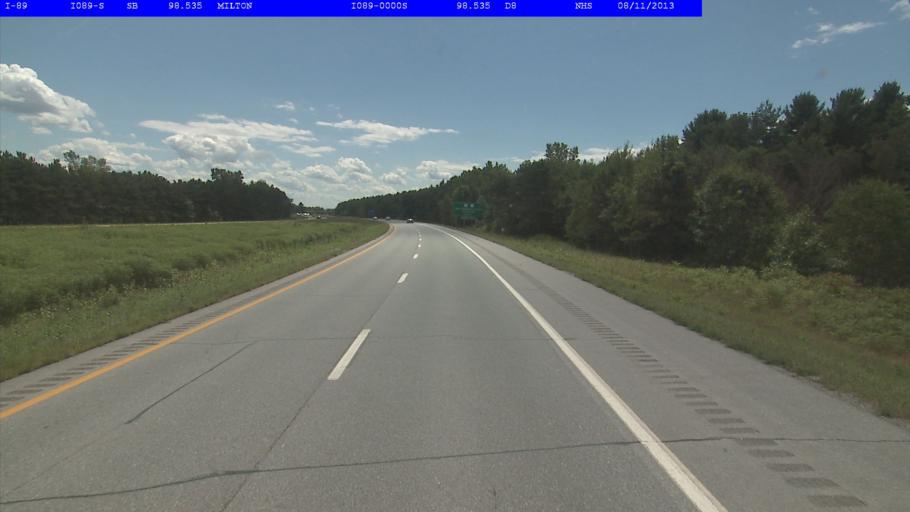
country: US
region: Vermont
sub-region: Chittenden County
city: Colchester
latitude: 44.5995
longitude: -73.1731
